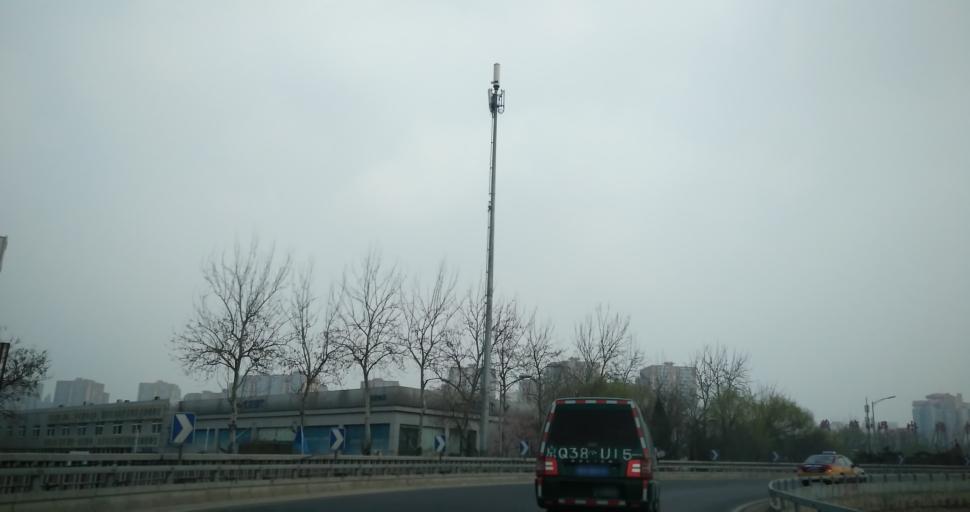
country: CN
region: Beijing
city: Longtan
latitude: 39.8614
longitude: 116.4469
